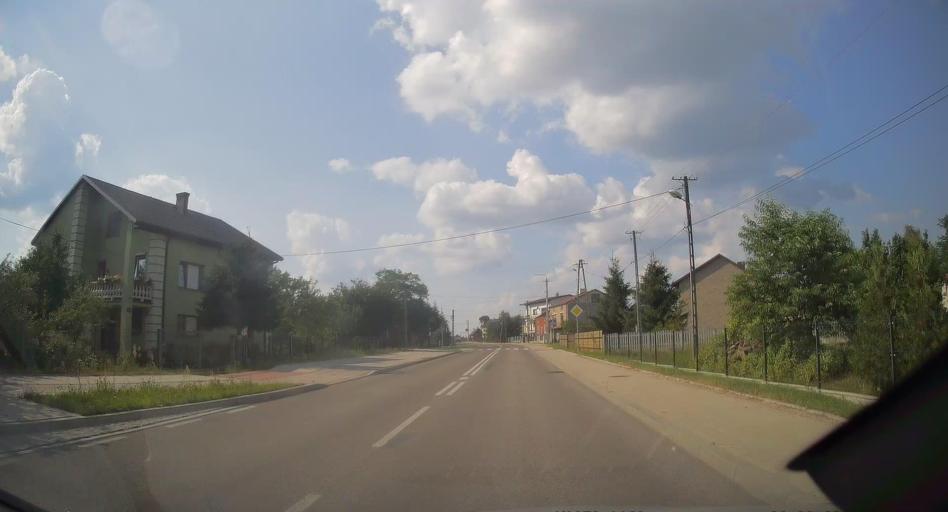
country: PL
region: Swietokrzyskie
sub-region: Powiat konecki
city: Radoszyce
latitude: 51.0629
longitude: 20.2748
